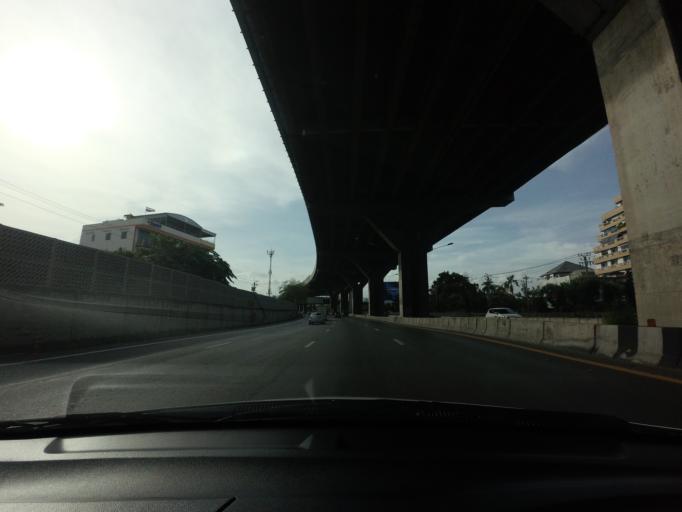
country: TH
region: Bangkok
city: Phra Khanong
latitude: 13.6917
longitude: 100.6006
